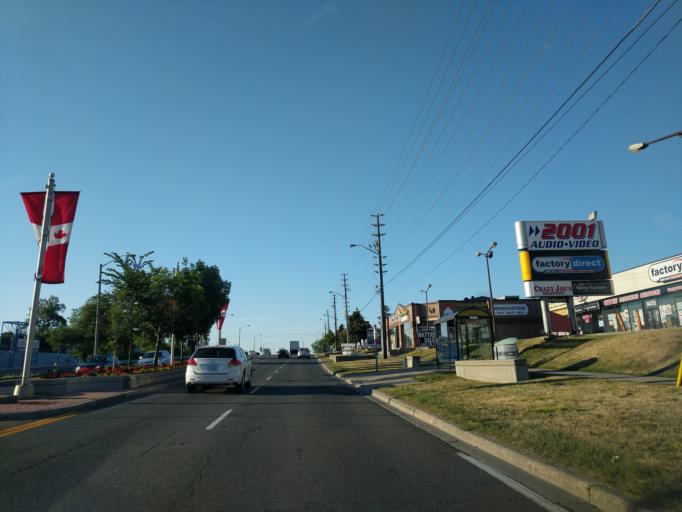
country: CA
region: Ontario
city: Scarborough
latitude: 43.7641
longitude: -79.2807
